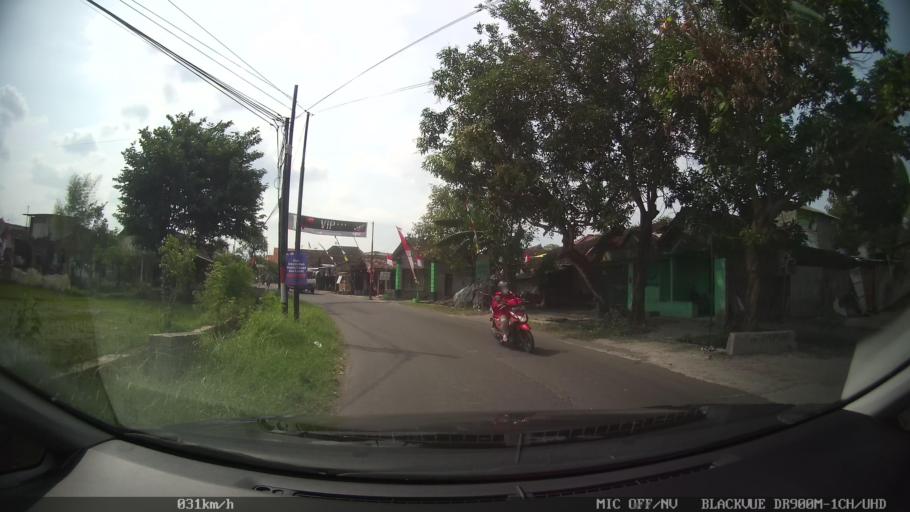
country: ID
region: Daerah Istimewa Yogyakarta
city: Depok
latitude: -7.8036
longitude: 110.4457
